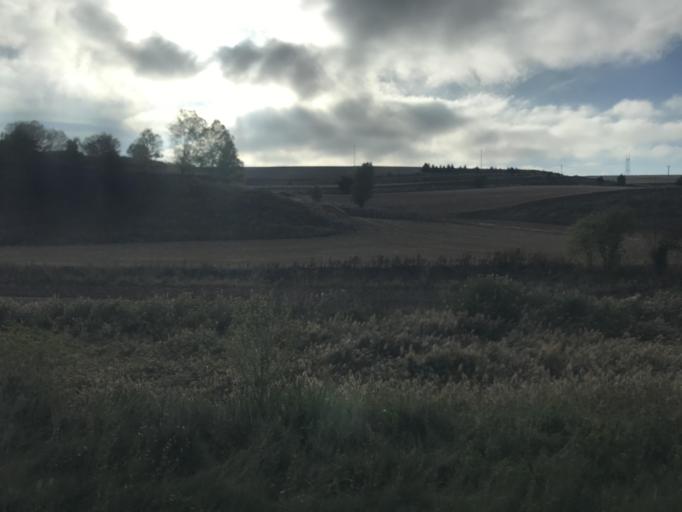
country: ES
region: Castille and Leon
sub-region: Provincia de Burgos
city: Buniel
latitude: 42.3232
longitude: -3.8171
